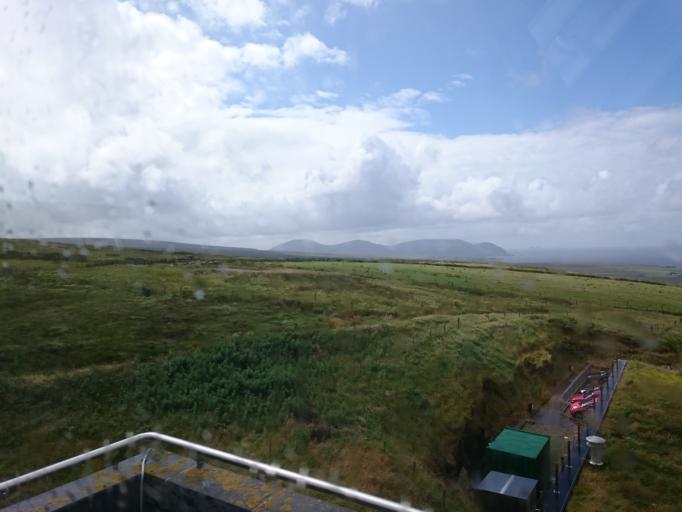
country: IE
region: Connaught
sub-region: Maigh Eo
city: Crossmolina
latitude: 54.3071
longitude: -9.4577
